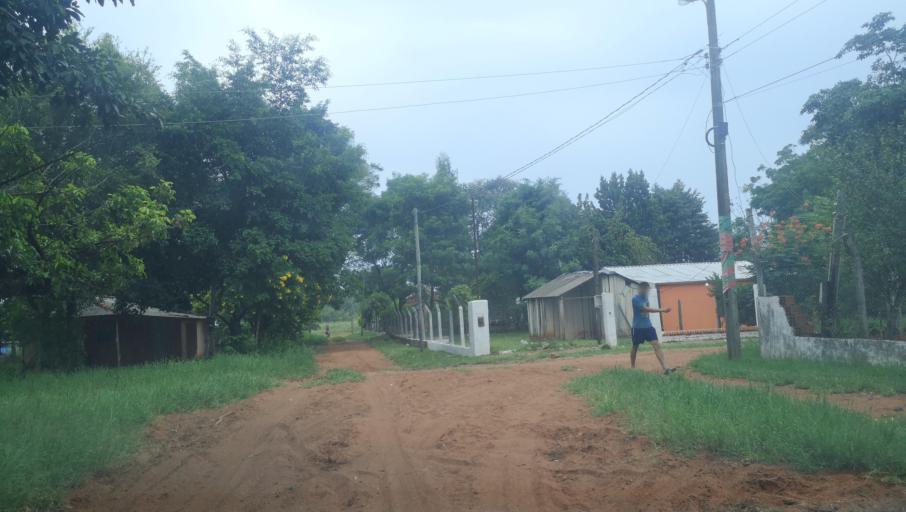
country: PY
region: San Pedro
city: Capiibary
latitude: -24.7285
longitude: -56.0118
